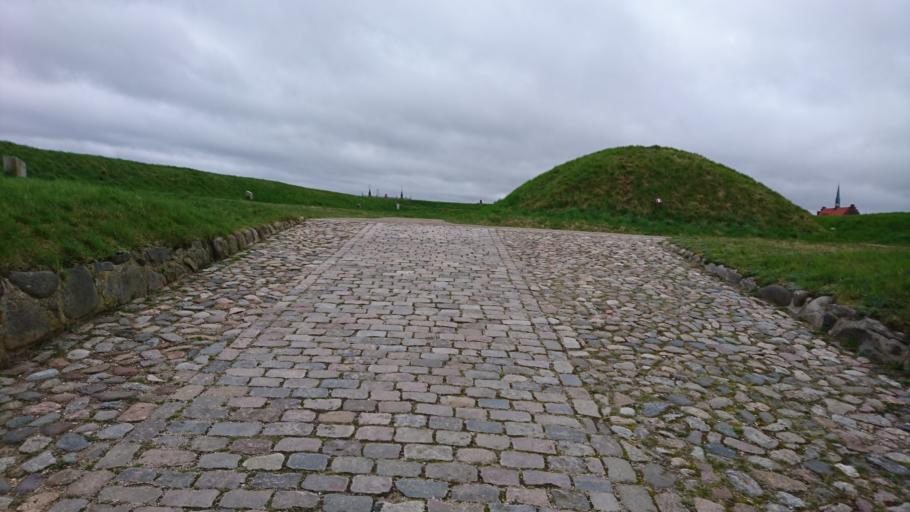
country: DK
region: Capital Region
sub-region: Helsingor Kommune
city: Helsingor
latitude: 56.0373
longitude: 12.6207
